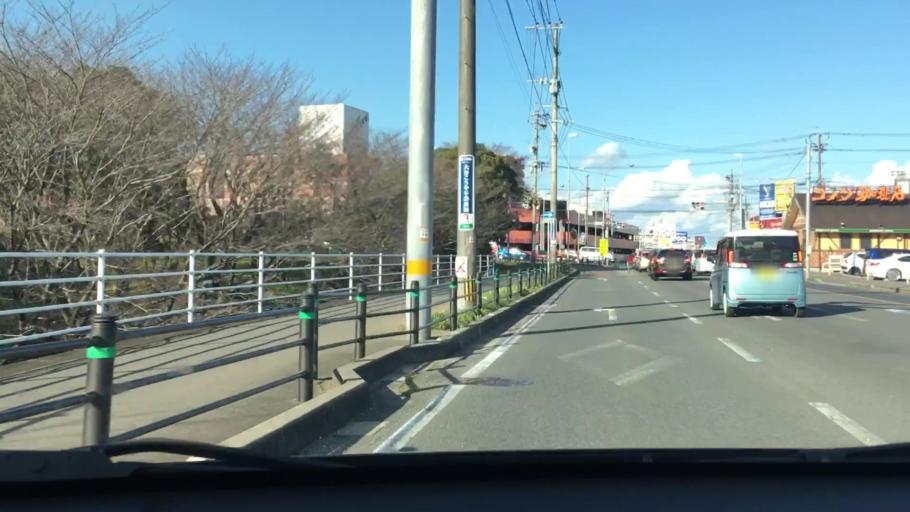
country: JP
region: Oita
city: Tsurusaki
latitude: 33.2243
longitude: 131.6592
